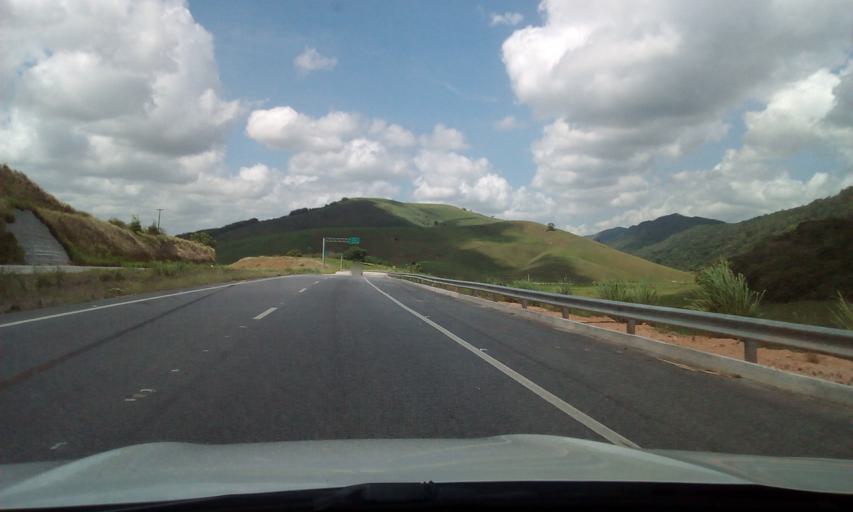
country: BR
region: Alagoas
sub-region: Flexeiras
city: Flexeiras
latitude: -9.2524
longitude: -35.7704
